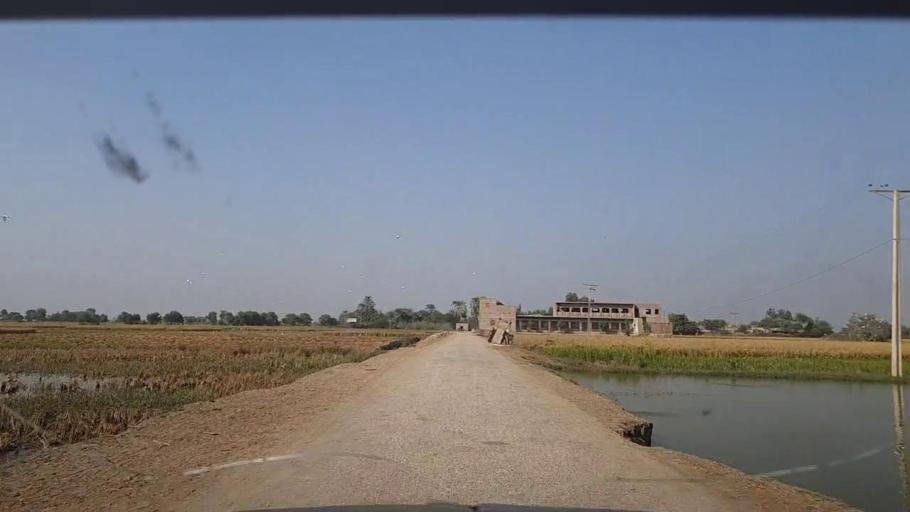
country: PK
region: Sindh
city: Shikarpur
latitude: 28.1180
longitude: 68.5788
